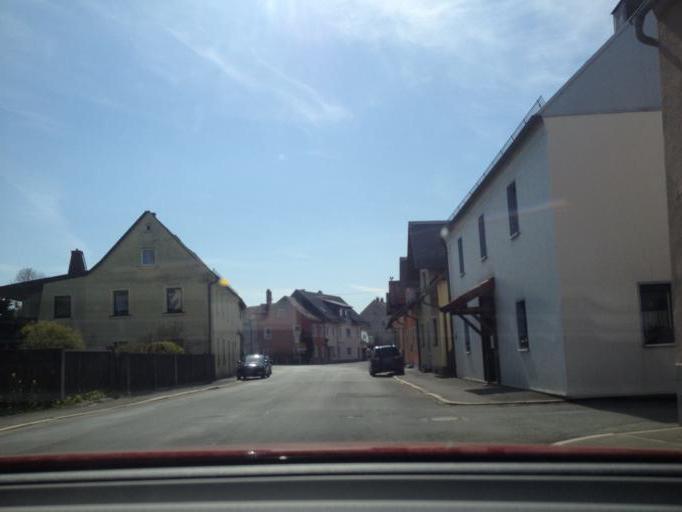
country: DE
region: Bavaria
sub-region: Upper Franconia
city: Thiersheim
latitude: 50.0757
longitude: 12.1298
